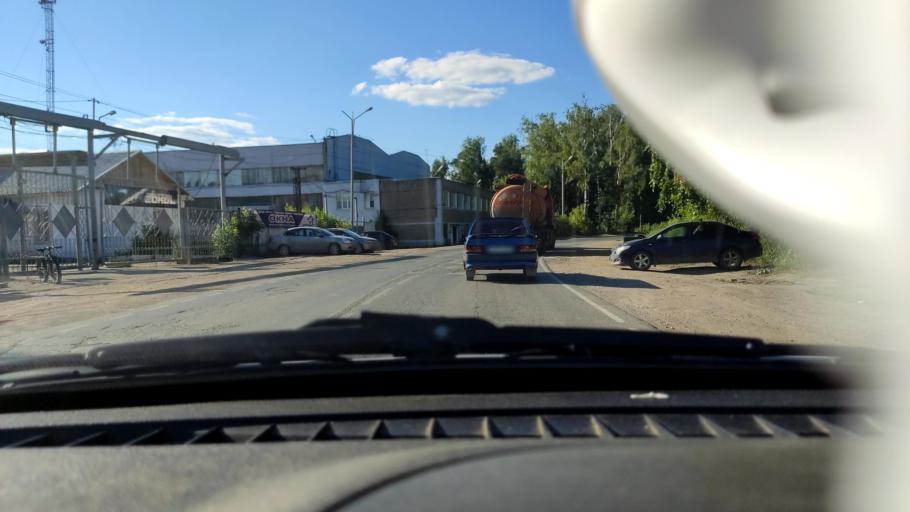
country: RU
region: Perm
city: Krasnokamsk
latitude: 58.0793
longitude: 55.7861
